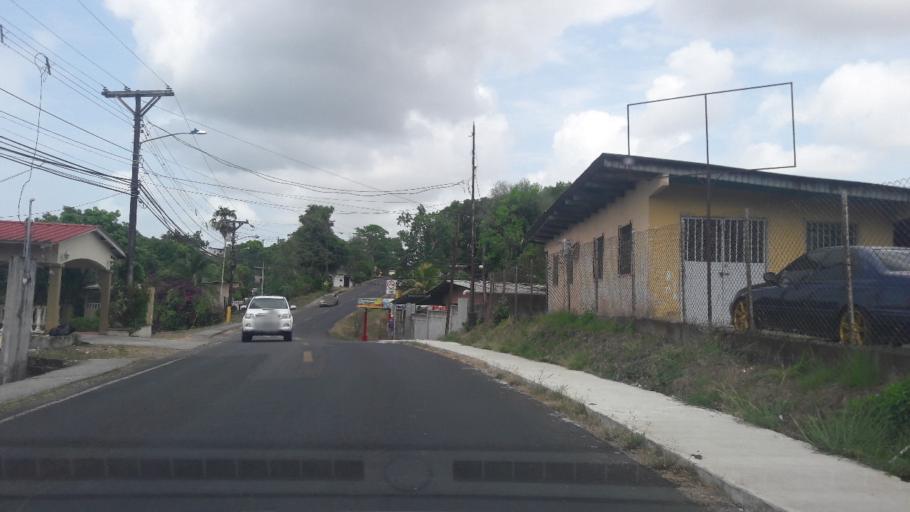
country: PA
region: Panama
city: Alcalde Diaz
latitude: 9.1158
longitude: -79.5549
